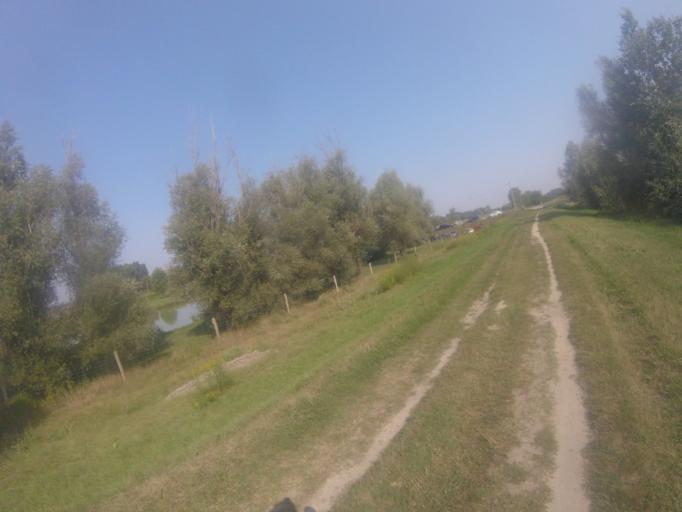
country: HU
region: Bacs-Kiskun
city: Baja
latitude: 46.2029
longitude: 18.9543
